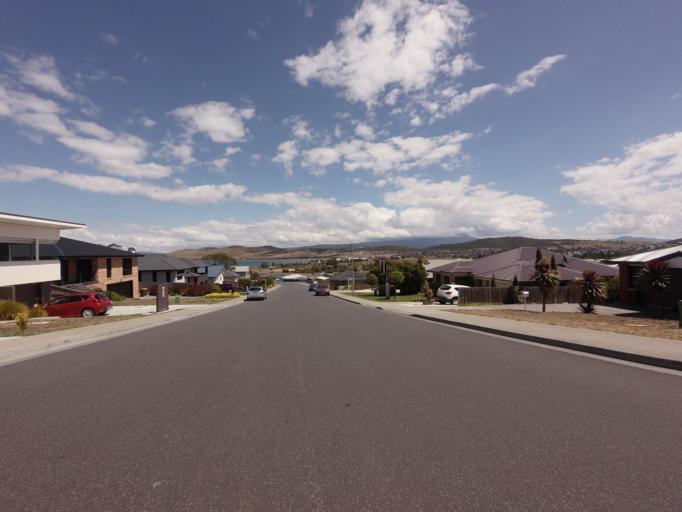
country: AU
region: Tasmania
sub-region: Clarence
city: Rokeby
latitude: -42.9042
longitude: 147.4580
